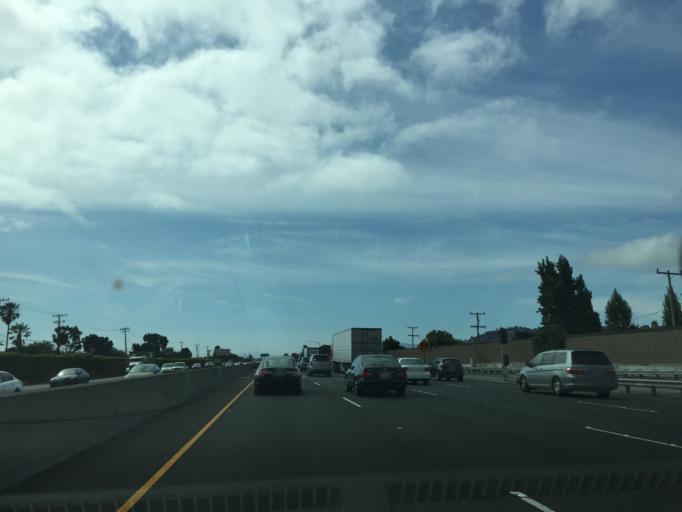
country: US
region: California
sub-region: San Mateo County
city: Foster City
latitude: 37.5417
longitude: -122.2854
